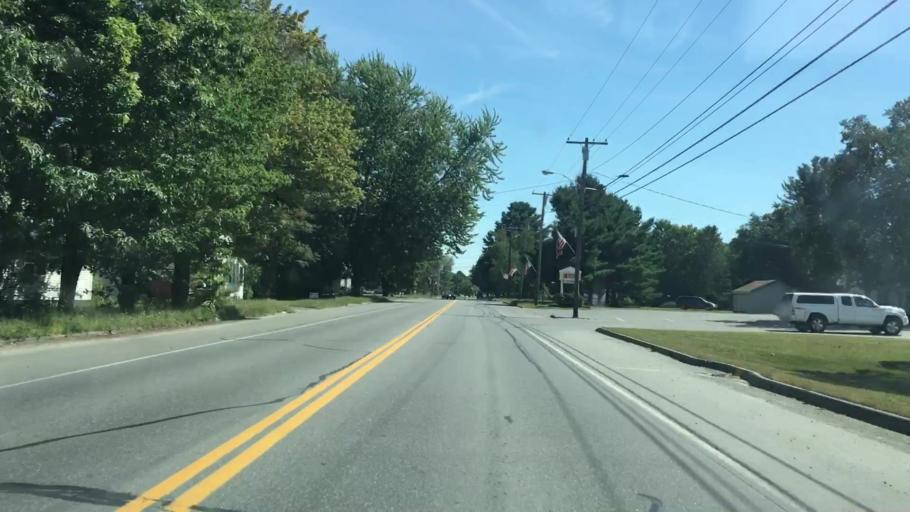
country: US
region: Maine
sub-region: Piscataquis County
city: Milo
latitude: 45.2635
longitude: -68.9912
